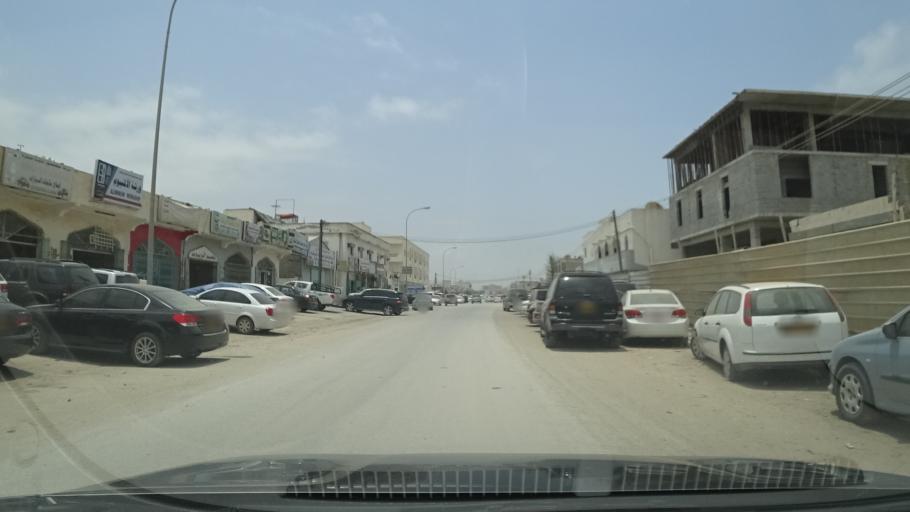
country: OM
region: Zufar
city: Salalah
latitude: 17.0189
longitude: 54.0509
